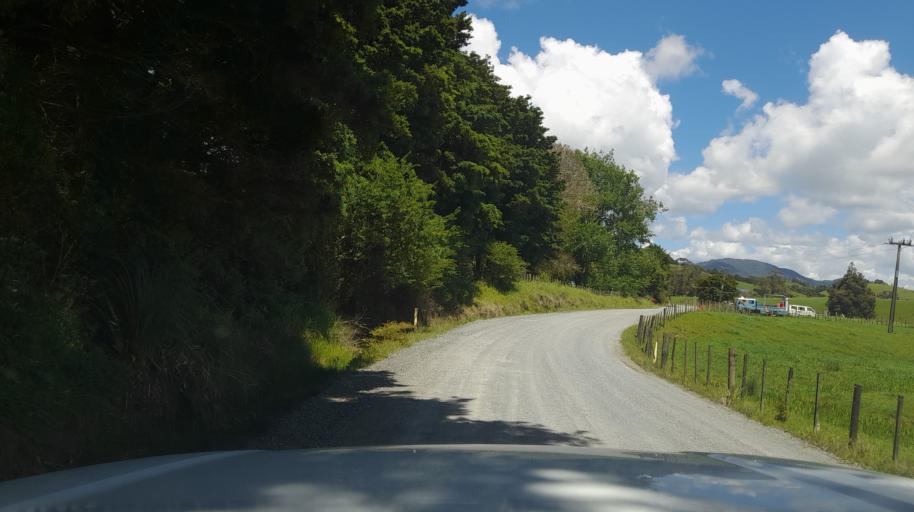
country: NZ
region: Northland
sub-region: Far North District
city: Kaitaia
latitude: -35.1094
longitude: 173.3952
